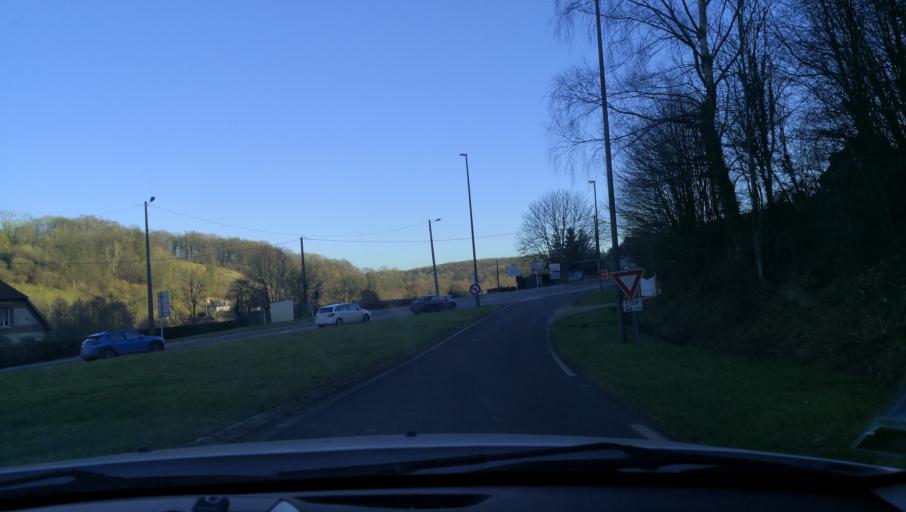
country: FR
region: Haute-Normandie
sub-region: Departement de la Seine-Maritime
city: Saint-Martin-Osmonville
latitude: 49.6455
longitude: 1.3014
